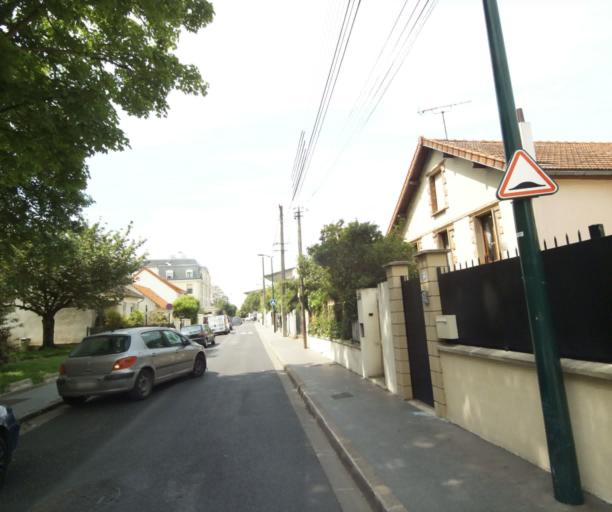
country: FR
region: Ile-de-France
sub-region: Departement des Hauts-de-Seine
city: Colombes
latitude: 48.9284
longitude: 2.2446
